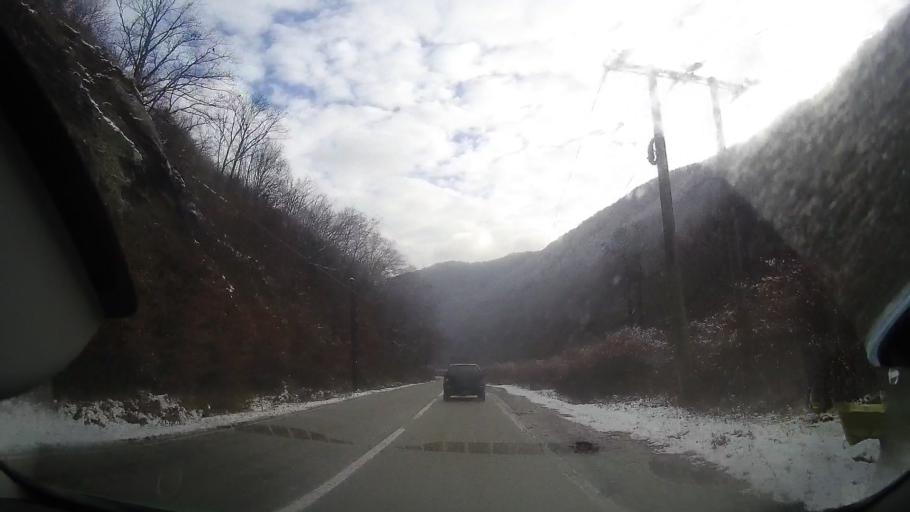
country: RO
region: Alba
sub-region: Oras Baia de Aries
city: Baia de Aries
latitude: 46.4040
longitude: 23.3413
